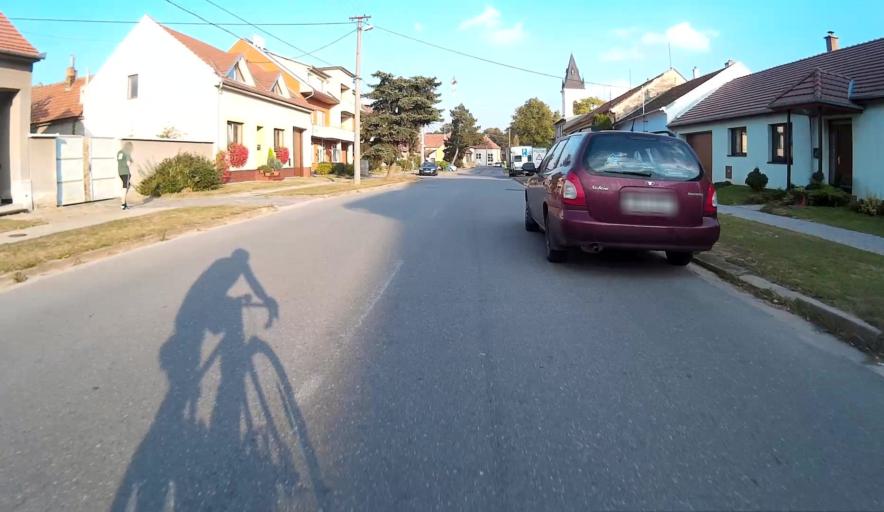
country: CZ
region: South Moravian
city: Podoli
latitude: 49.1907
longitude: 16.7244
